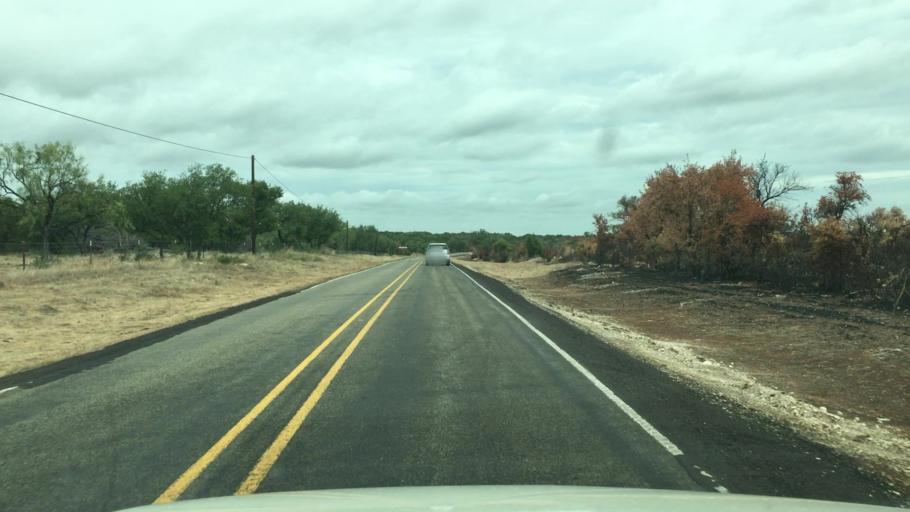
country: US
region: Texas
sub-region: Llano County
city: Horseshoe Bay
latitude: 30.4823
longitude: -98.4258
